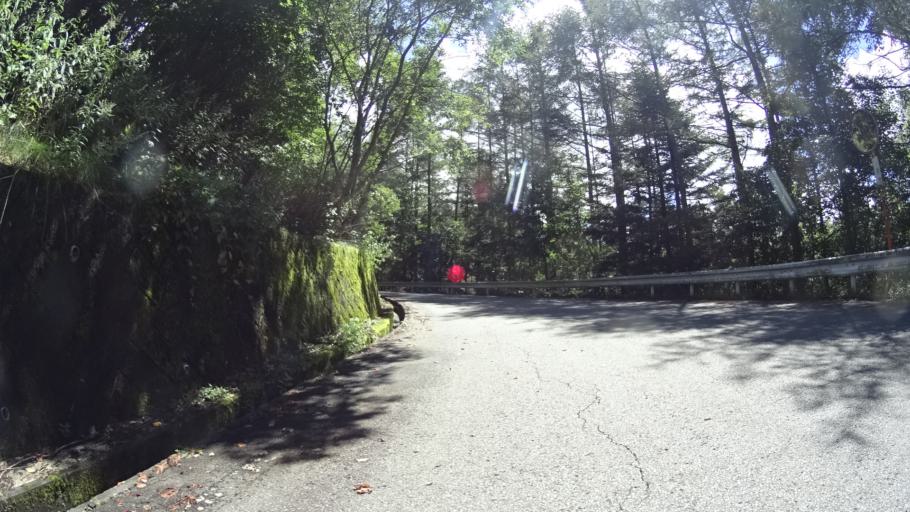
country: JP
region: Yamanashi
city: Enzan
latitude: 35.7227
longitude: 138.8408
